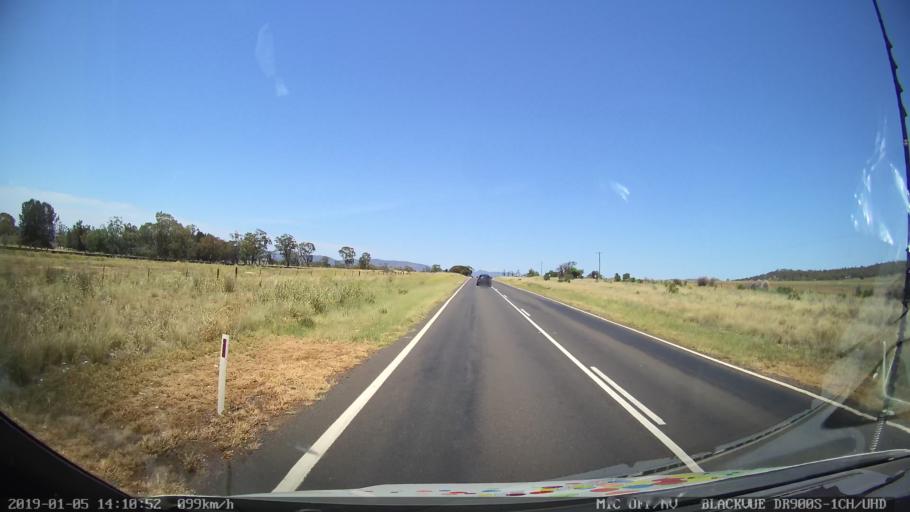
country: AU
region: New South Wales
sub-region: Gunnedah
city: Gunnedah
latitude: -31.2447
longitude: 150.4497
